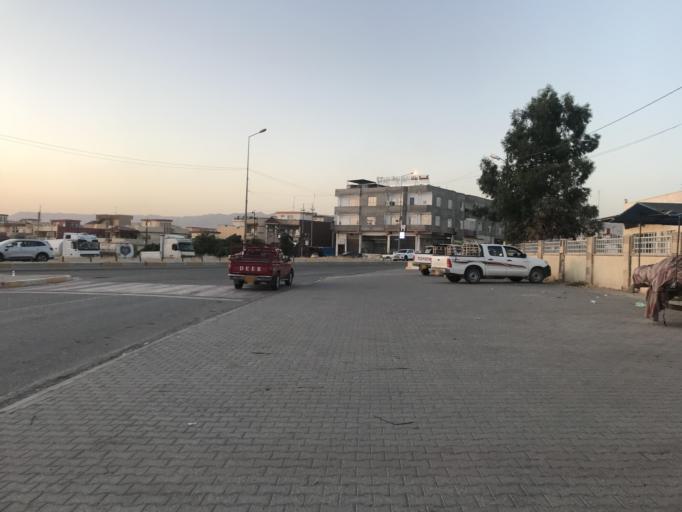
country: IQ
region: Dahuk
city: Saymayl
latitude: 36.8606
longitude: 42.8365
